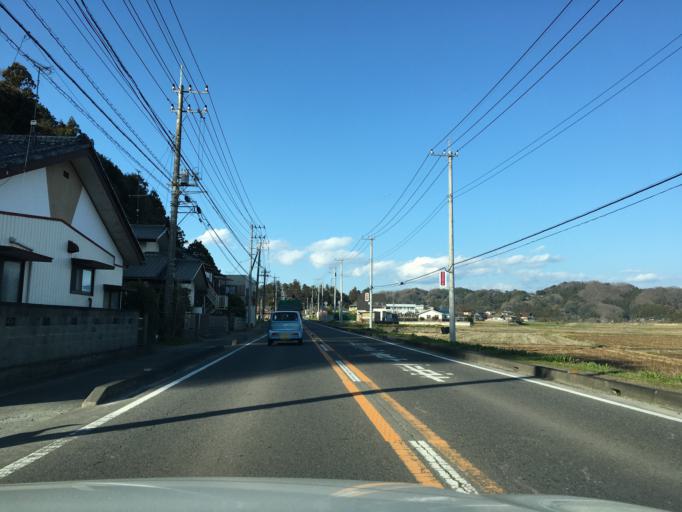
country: JP
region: Ibaraki
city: Omiya
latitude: 36.5898
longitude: 140.4110
